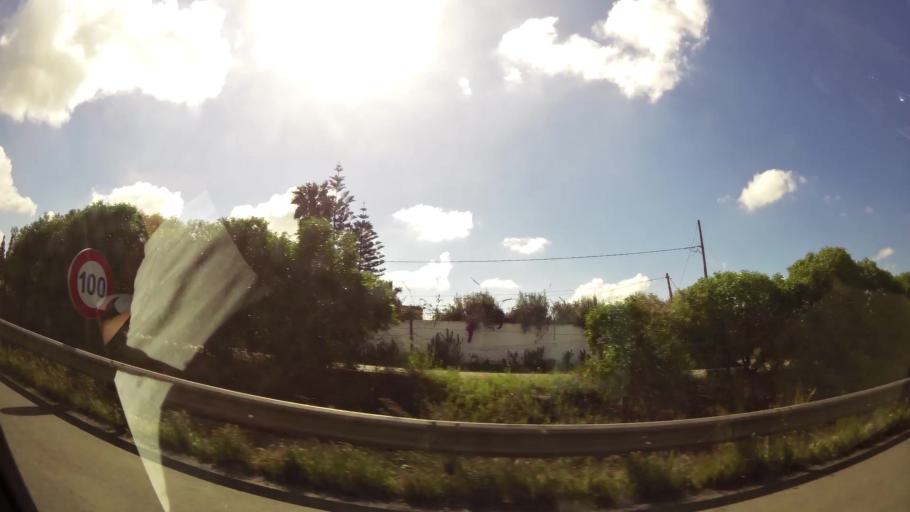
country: MA
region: Grand Casablanca
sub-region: Nouaceur
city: Bouskoura
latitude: 33.4524
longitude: -7.6335
